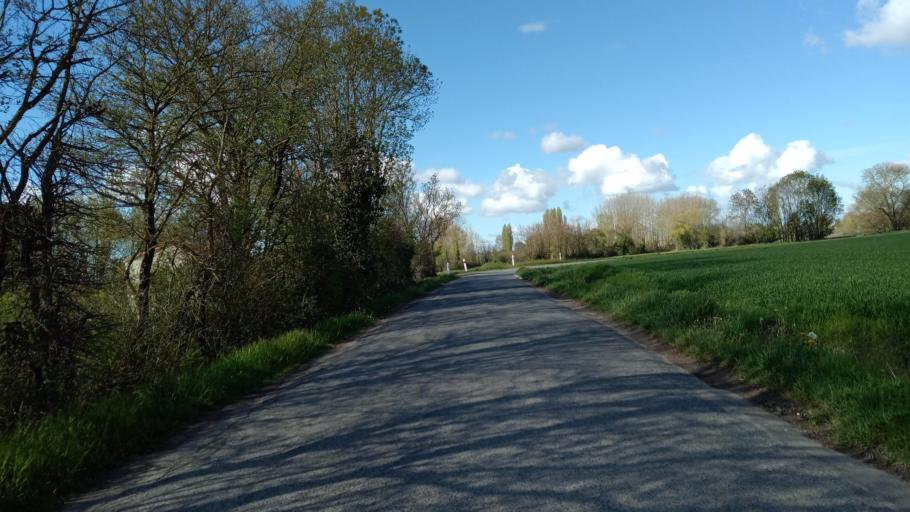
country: FR
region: Poitou-Charentes
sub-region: Departement de la Charente-Maritime
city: Verines
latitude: 46.1492
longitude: -0.9363
